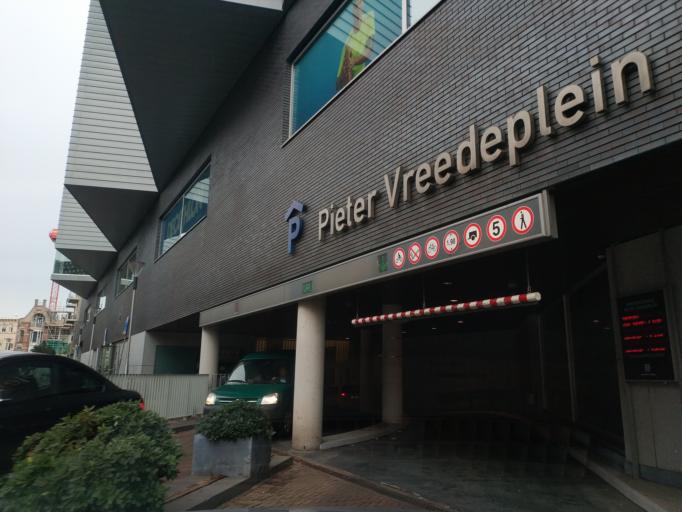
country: NL
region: North Brabant
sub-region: Gemeente Tilburg
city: Tilburg
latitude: 51.5584
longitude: 5.0889
